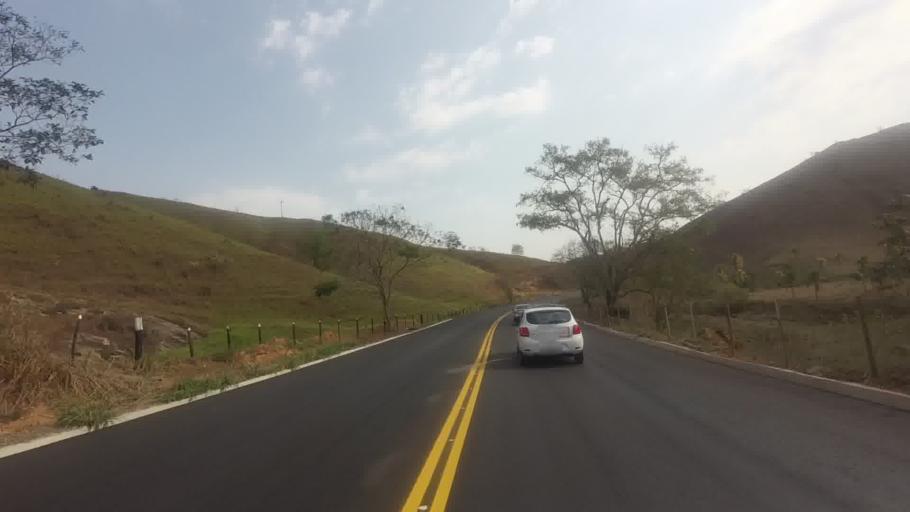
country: BR
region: Rio de Janeiro
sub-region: Bom Jesus Do Itabapoana
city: Bom Jesus do Itabapoana
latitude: -21.2151
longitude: -41.7359
